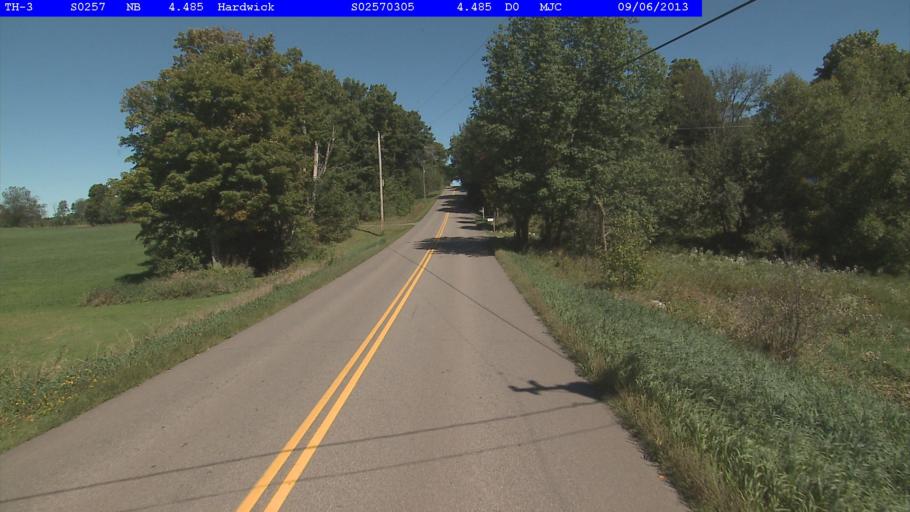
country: US
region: Vermont
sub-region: Caledonia County
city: Hardwick
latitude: 44.5519
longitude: -72.3190
